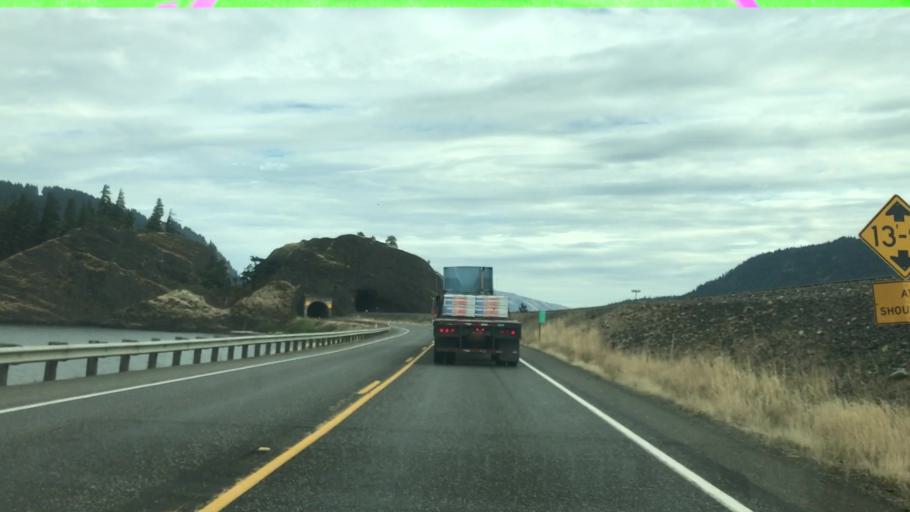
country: US
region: Oregon
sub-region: Hood River County
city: Hood River
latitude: 45.7103
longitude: -121.6285
